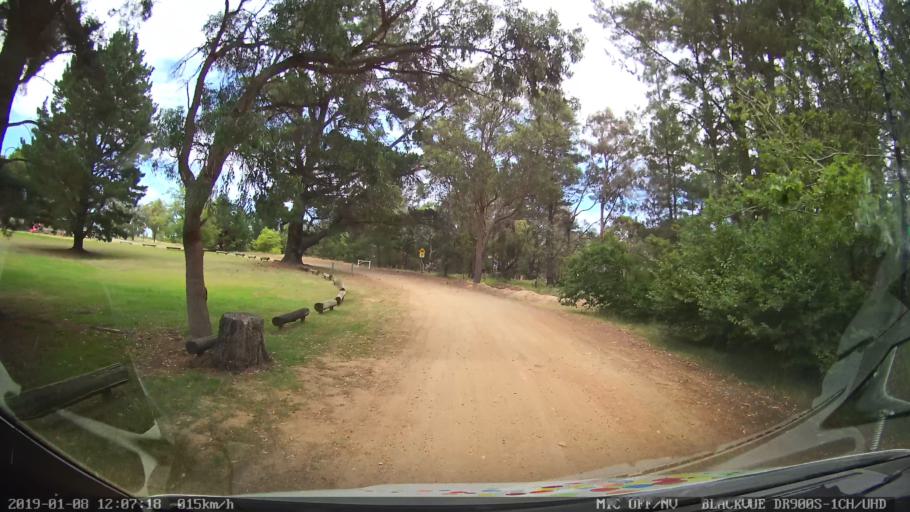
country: AU
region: New South Wales
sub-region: Armidale Dumaresq
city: Armidale
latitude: -30.4266
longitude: 151.5940
